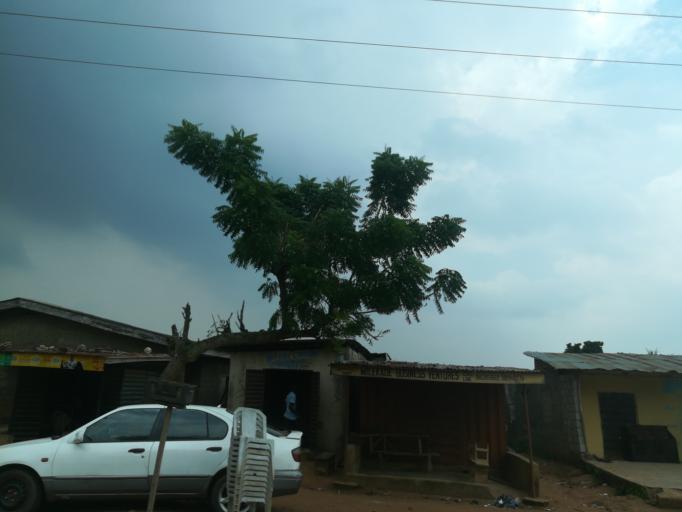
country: NG
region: Lagos
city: Ikorodu
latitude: 6.6023
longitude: 3.5874
